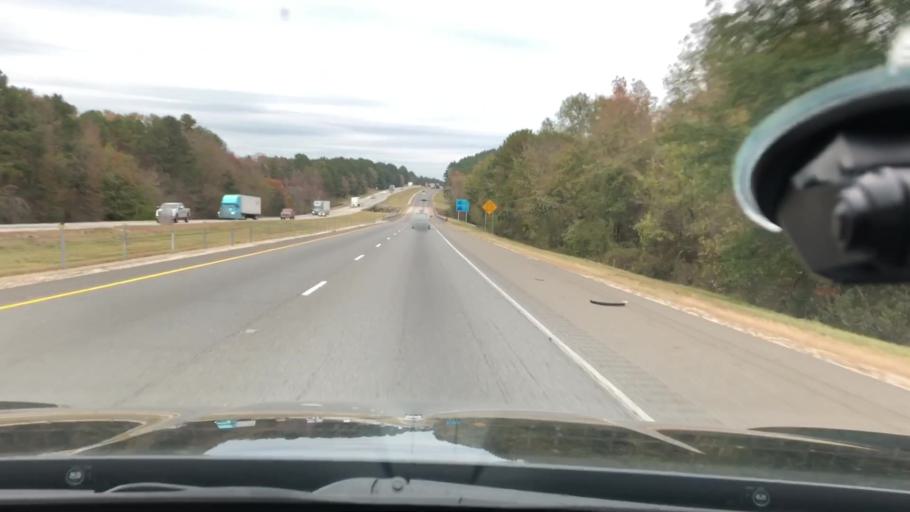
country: US
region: Arkansas
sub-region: Hot Spring County
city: Malvern
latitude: 34.3146
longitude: -92.9362
